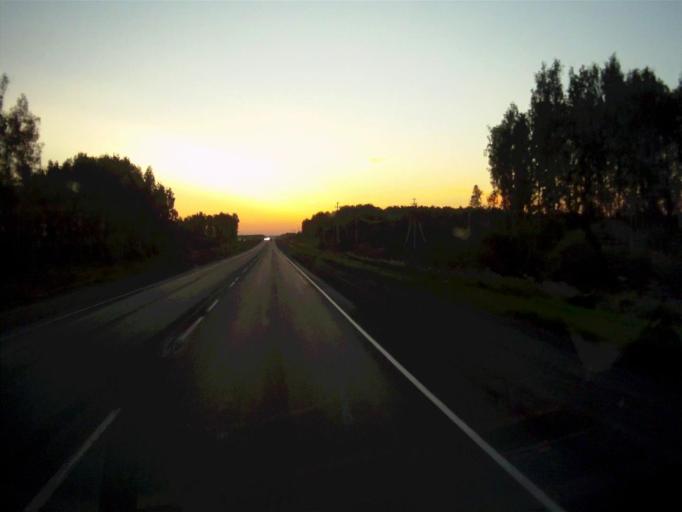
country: RU
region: Chelyabinsk
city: Poletayevo
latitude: 55.2121
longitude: 61.0722
